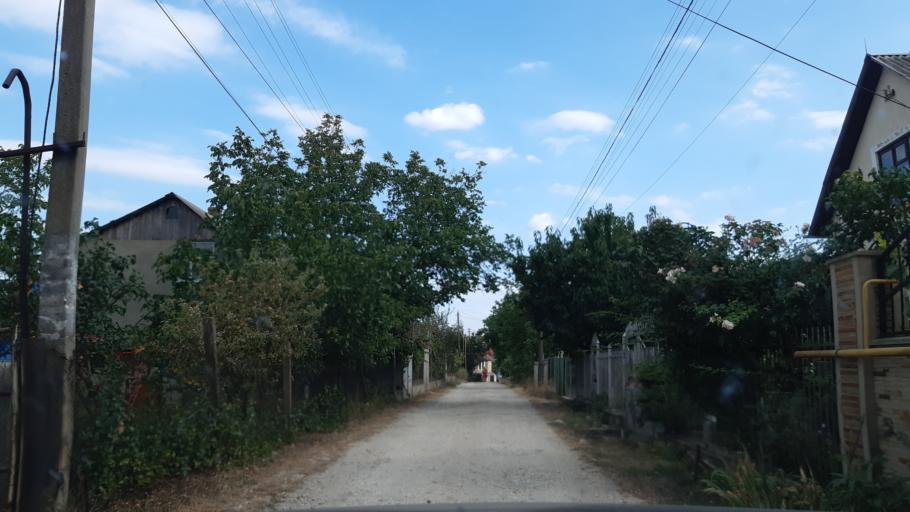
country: MD
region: Chisinau
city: Vatra
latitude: 47.0462
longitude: 28.7339
